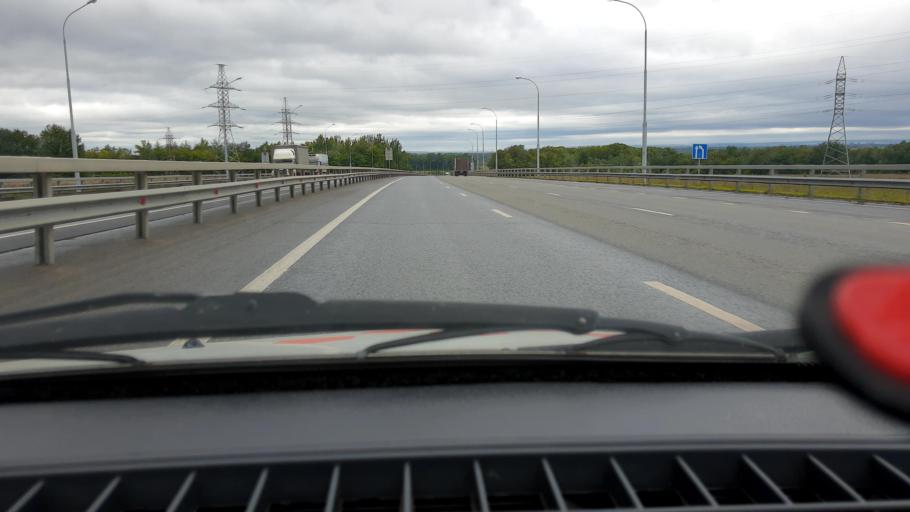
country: RU
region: Bashkortostan
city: Kabakovo
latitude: 54.6524
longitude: 56.1111
